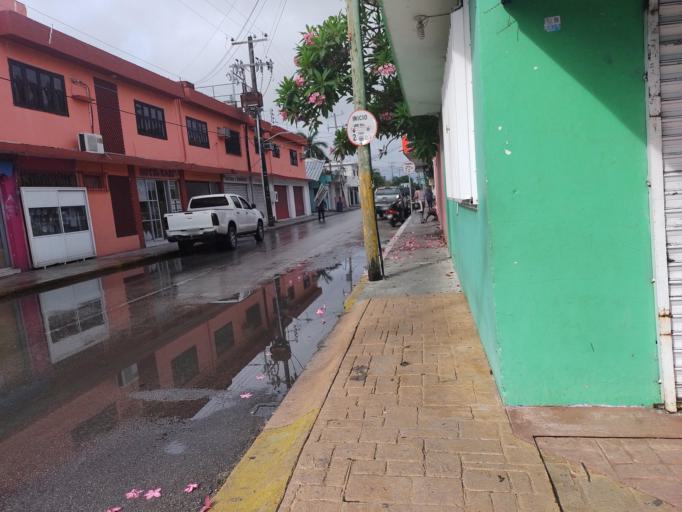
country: MX
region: Quintana Roo
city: San Miguel de Cozumel
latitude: 20.5061
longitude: -86.9473
